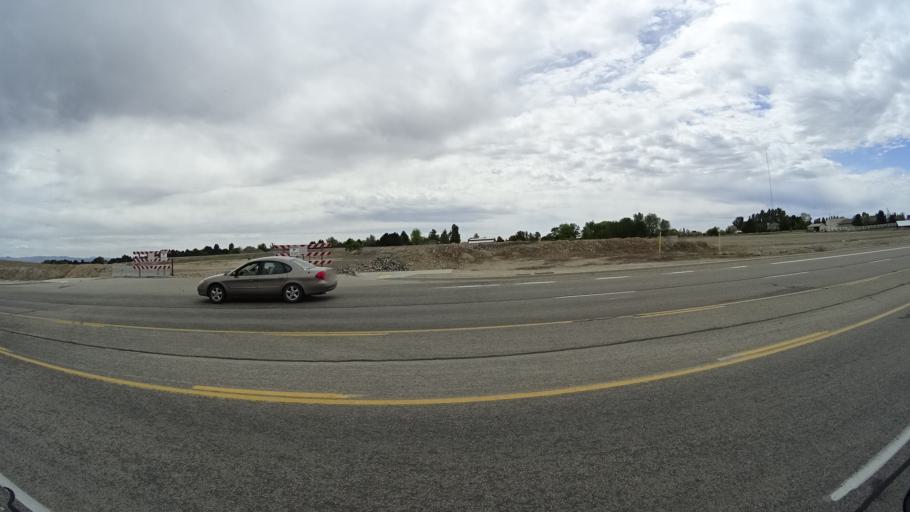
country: US
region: Idaho
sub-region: Ada County
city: Meridian
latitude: 43.5853
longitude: -116.4303
